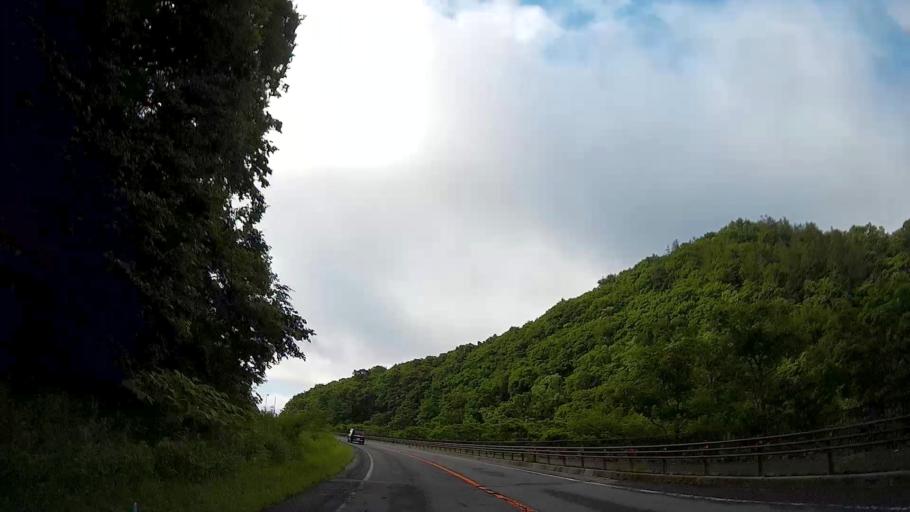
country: JP
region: Hokkaido
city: Date
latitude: 42.5603
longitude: 140.8862
